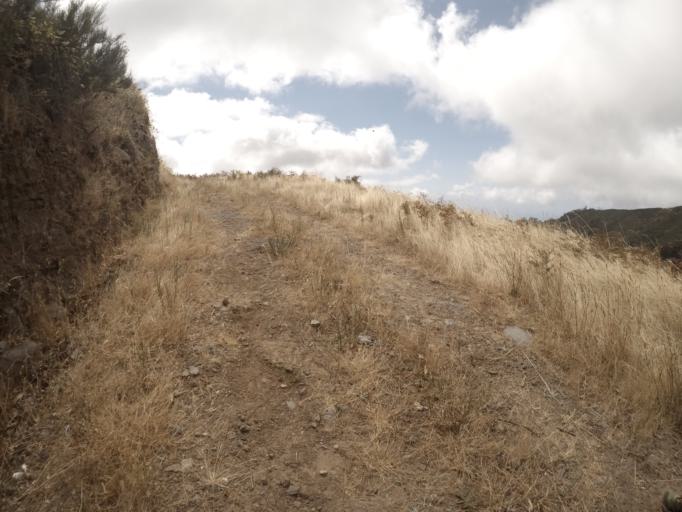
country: PT
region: Madeira
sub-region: Camara de Lobos
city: Curral das Freiras
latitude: 32.7103
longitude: -16.9988
